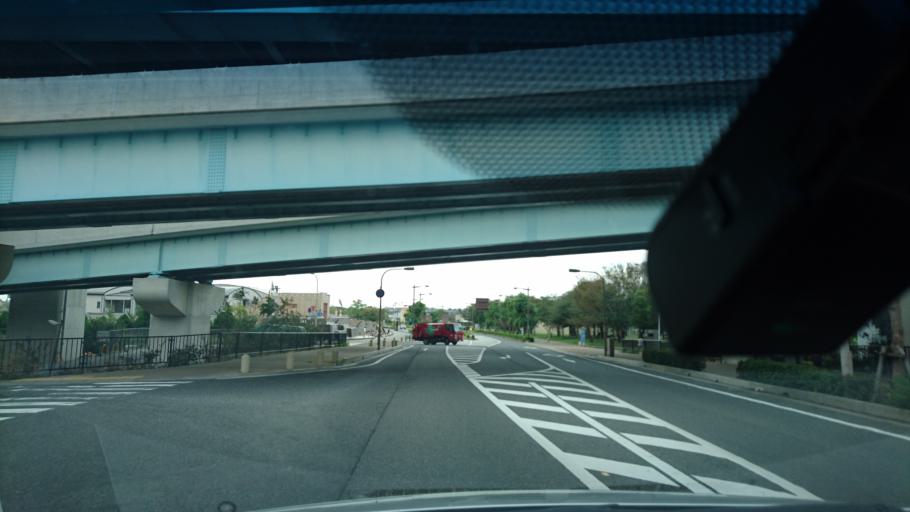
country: JP
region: Hyogo
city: Ashiya
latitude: 34.7135
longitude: 135.3090
